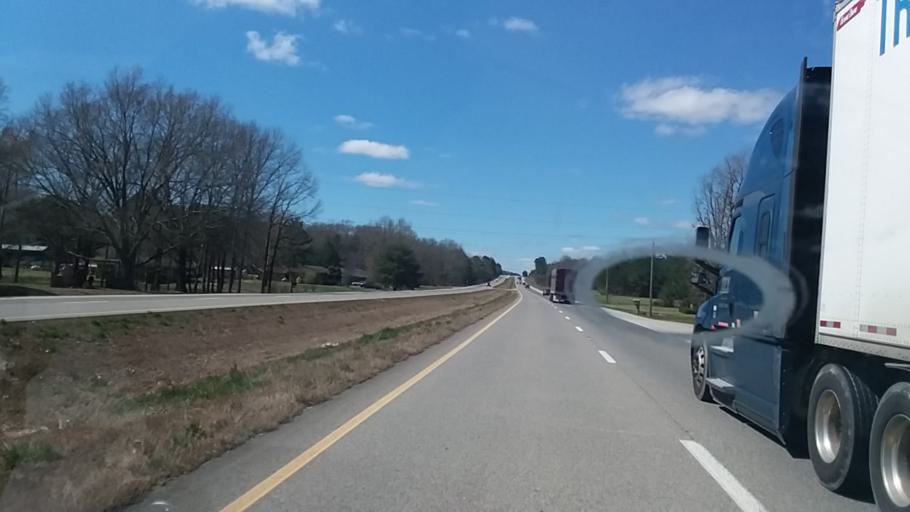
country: US
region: Alabama
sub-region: Colbert County
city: Cherokee
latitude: 34.7427
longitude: -87.9275
